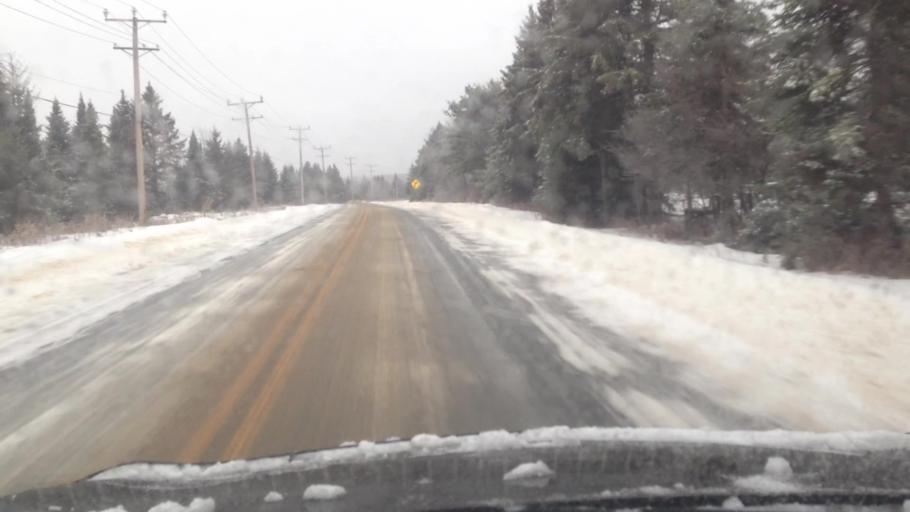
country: CA
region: Quebec
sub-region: Laurentides
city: Mont-Tremblant
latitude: 45.9940
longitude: -74.6227
